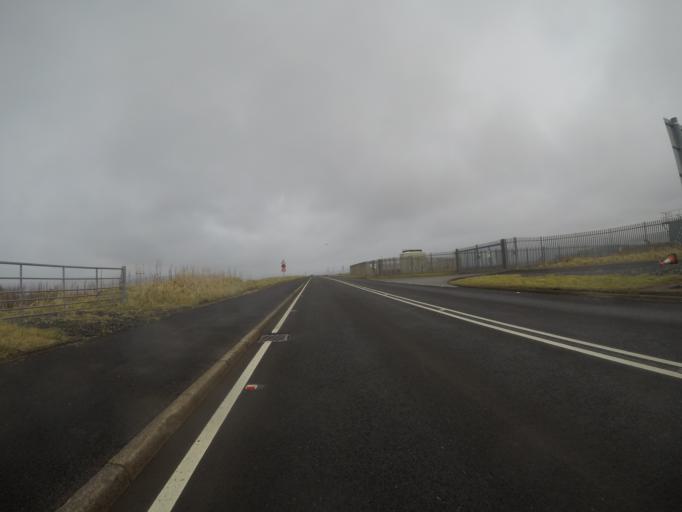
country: GB
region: Scotland
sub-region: North Ayrshire
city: Millport
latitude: 55.7237
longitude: -4.8985
